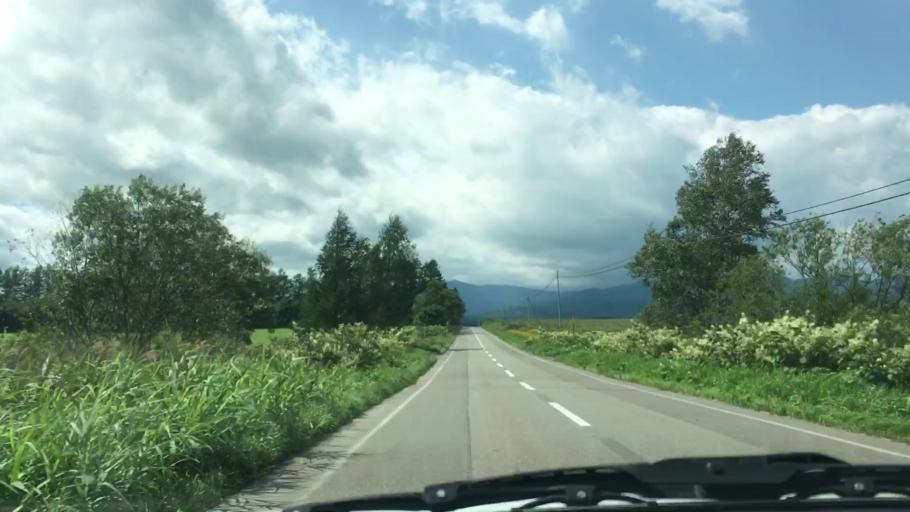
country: JP
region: Hokkaido
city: Otofuke
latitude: 43.2792
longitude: 143.3489
